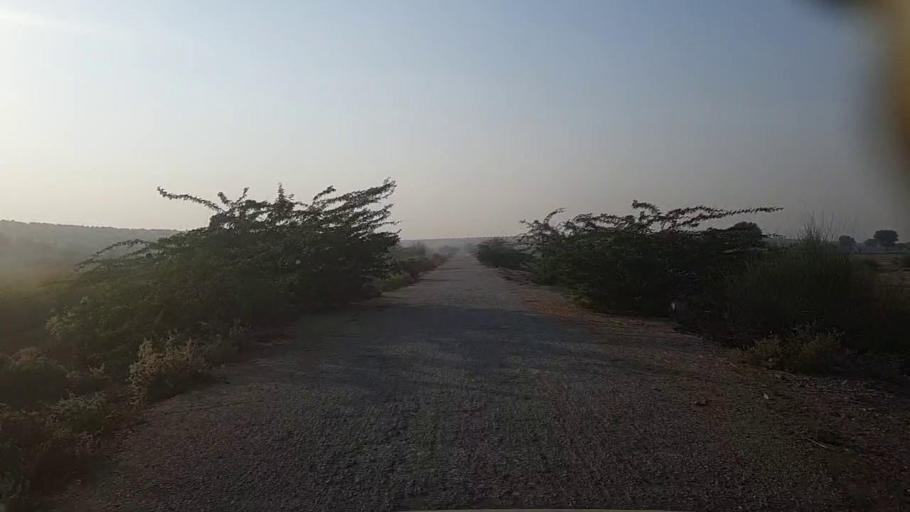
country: PK
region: Sindh
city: Pad Idan
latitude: 26.7219
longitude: 68.4465
